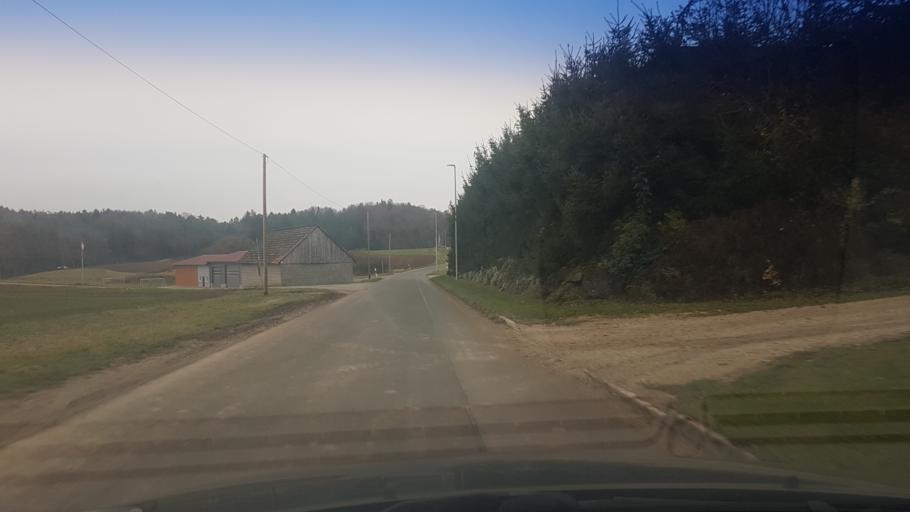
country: DE
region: Bavaria
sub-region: Upper Franconia
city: Stadelhofen
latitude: 50.0297
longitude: 11.2354
